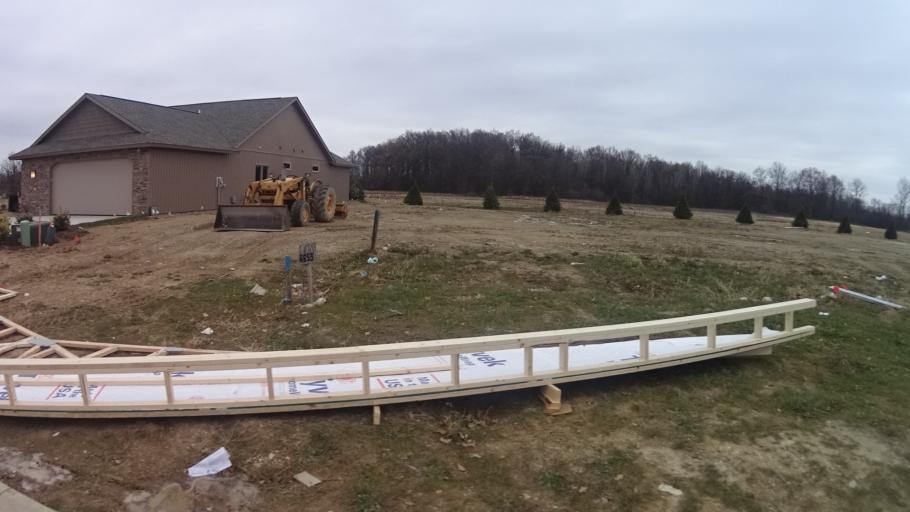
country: US
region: Ohio
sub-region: Lorain County
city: North Ridgeville
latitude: 41.3582
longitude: -81.9812
